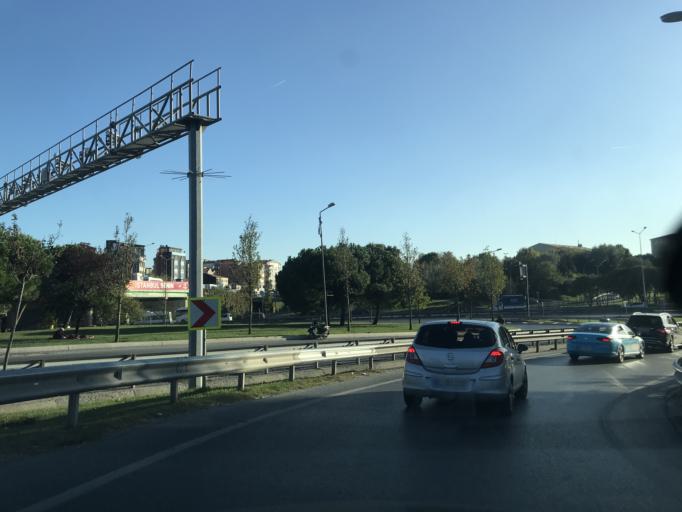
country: TR
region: Istanbul
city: Sisli
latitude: 41.0562
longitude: 28.9621
